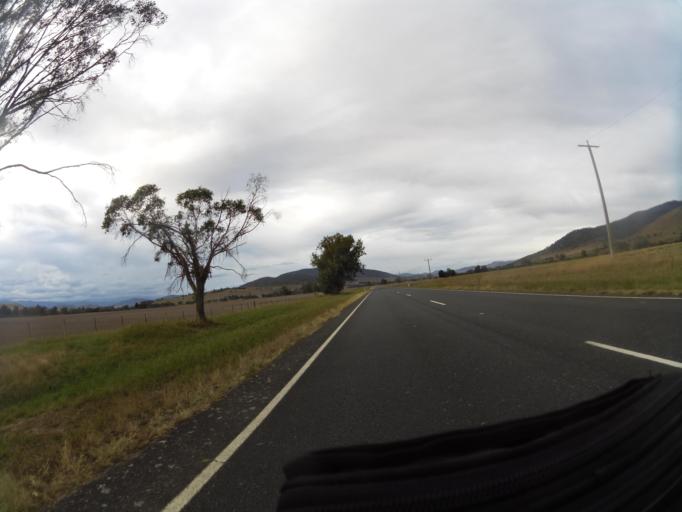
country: AU
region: New South Wales
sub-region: Snowy River
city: Jindabyne
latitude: -36.1052
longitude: 147.9803
